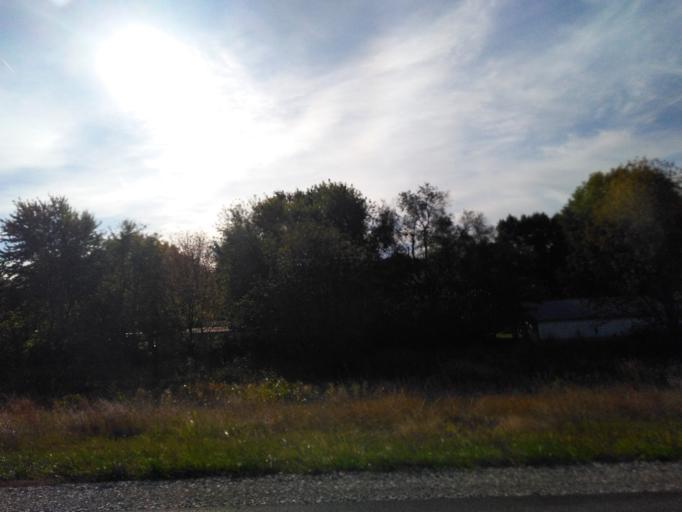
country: US
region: Illinois
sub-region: Saint Clair County
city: Dupo
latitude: 38.5353
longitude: -90.1882
